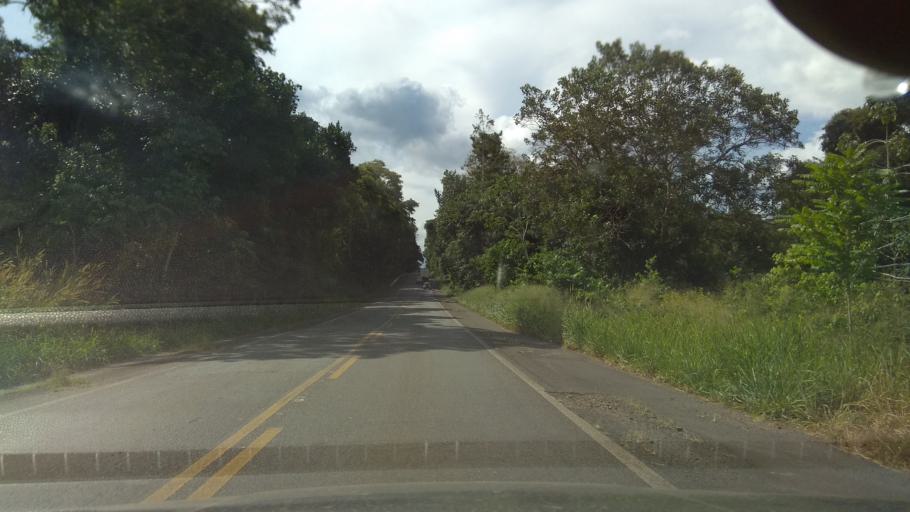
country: BR
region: Bahia
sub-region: Itajuipe
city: Itajuipe
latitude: -14.6334
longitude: -39.3349
